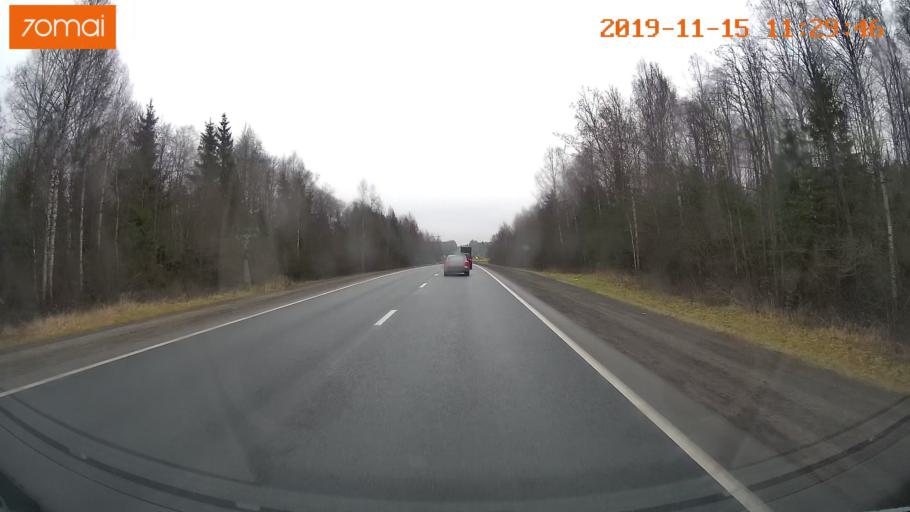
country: RU
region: Vologda
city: Molochnoye
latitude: 59.1765
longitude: 39.5183
